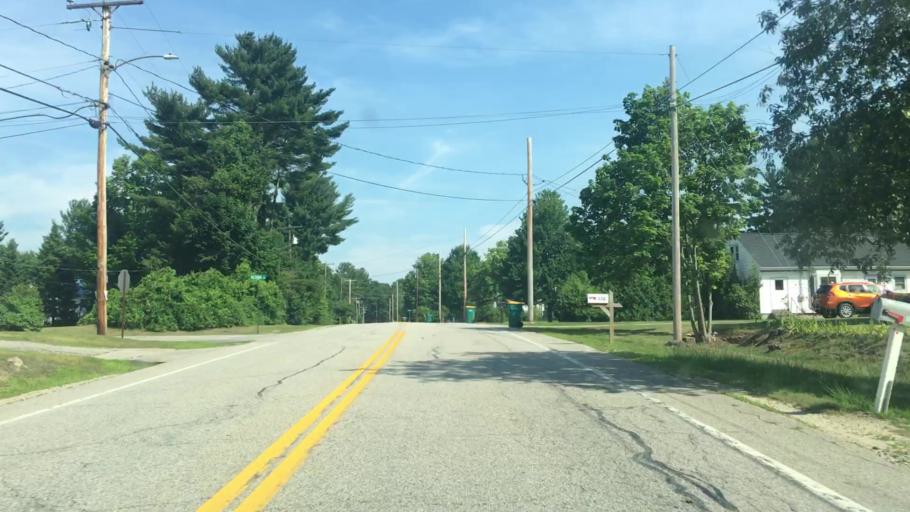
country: US
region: New Hampshire
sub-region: Strafford County
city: Rochester
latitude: 43.2769
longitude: -70.9632
